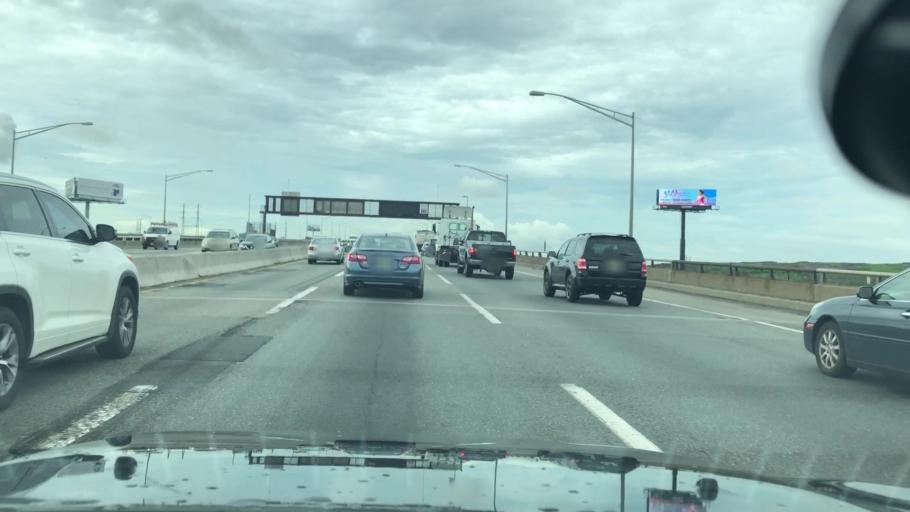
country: US
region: New Jersey
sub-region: Hudson County
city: Kearny
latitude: 40.7512
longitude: -74.1195
